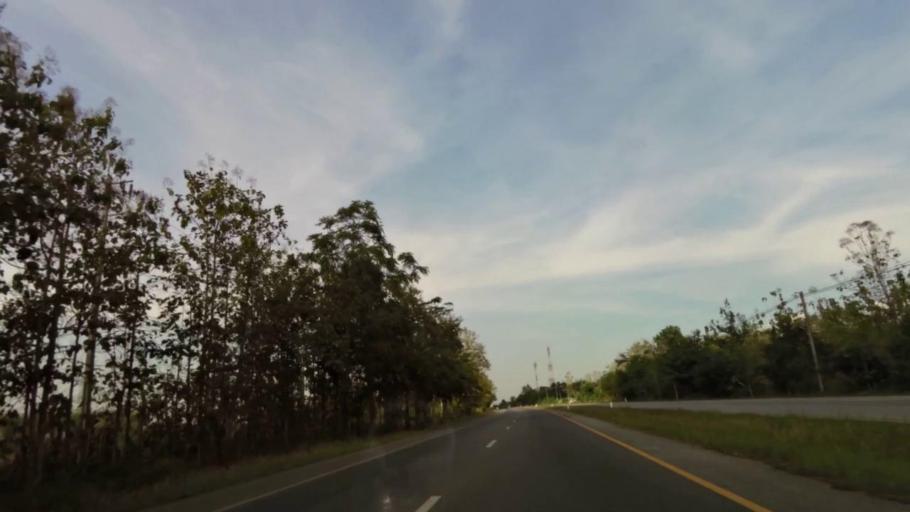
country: TH
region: Uttaradit
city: Tron
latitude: 17.5292
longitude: 100.2121
